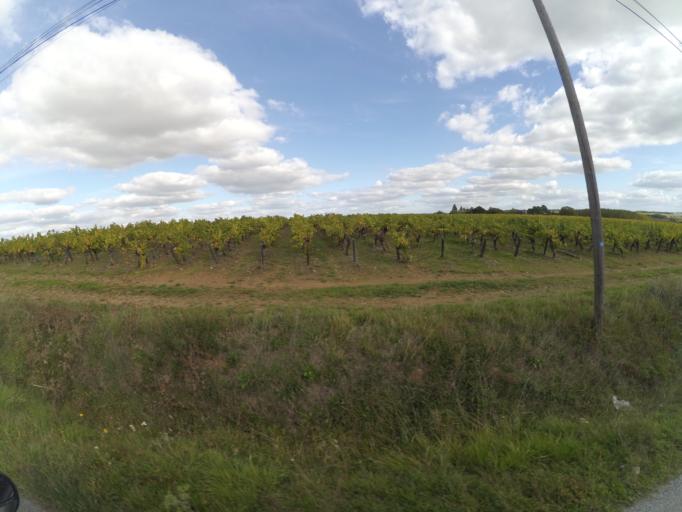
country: FR
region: Pays de la Loire
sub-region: Departement de la Loire-Atlantique
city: Le Loroux-Bottereau
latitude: 47.2155
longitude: -1.3576
